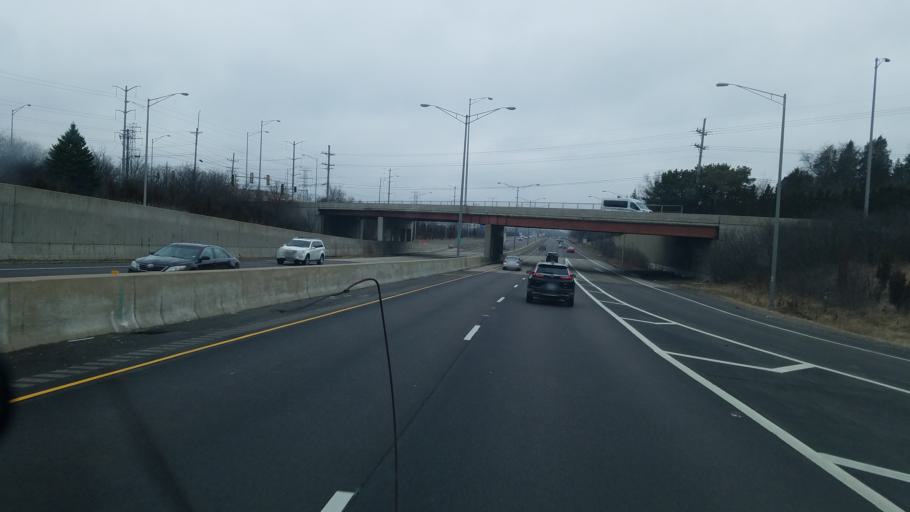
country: US
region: Illinois
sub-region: Lake County
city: Highland Park
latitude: 42.1592
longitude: -87.8052
